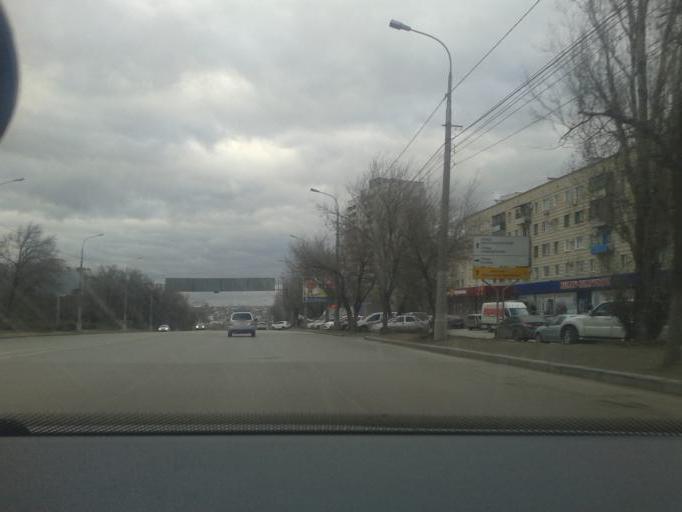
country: RU
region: Volgograd
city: Volgograd
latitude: 48.6763
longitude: 44.4444
